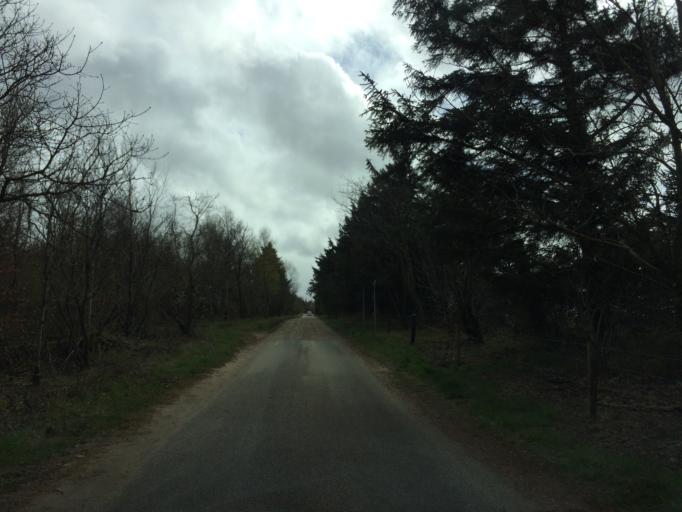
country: DK
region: South Denmark
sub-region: Varde Kommune
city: Oksbol
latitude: 55.5703
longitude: 8.3088
